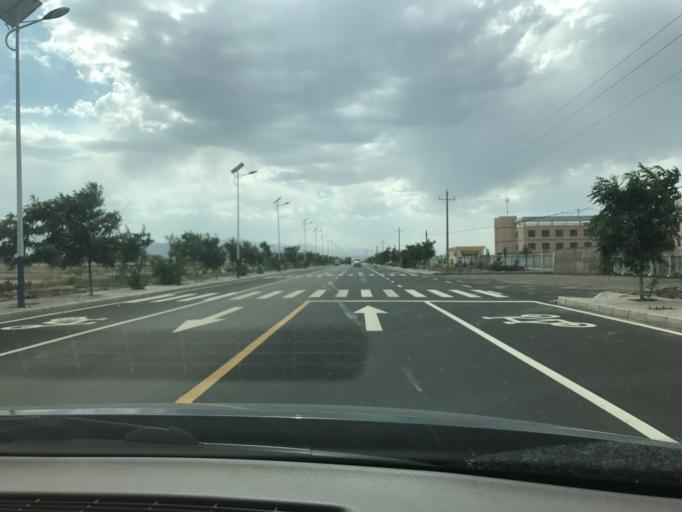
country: CN
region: Gansu Sheng
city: Wuwei
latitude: 38.1031
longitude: 102.4421
